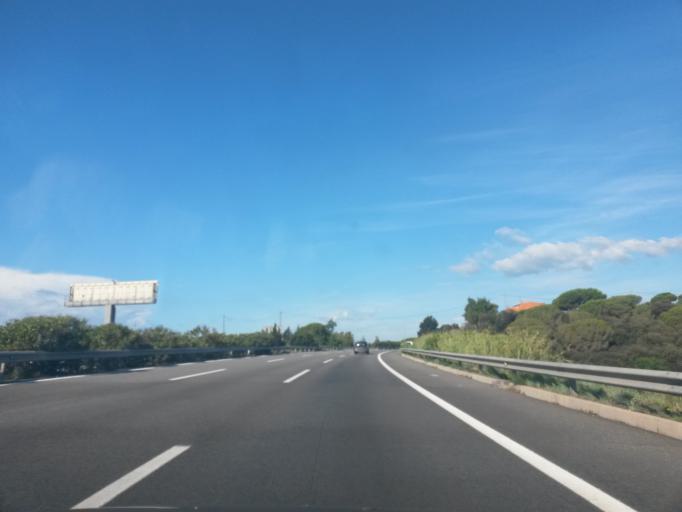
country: ES
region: Catalonia
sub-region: Provincia de Barcelona
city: Arenys de Mar
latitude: 41.5914
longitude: 2.5577
